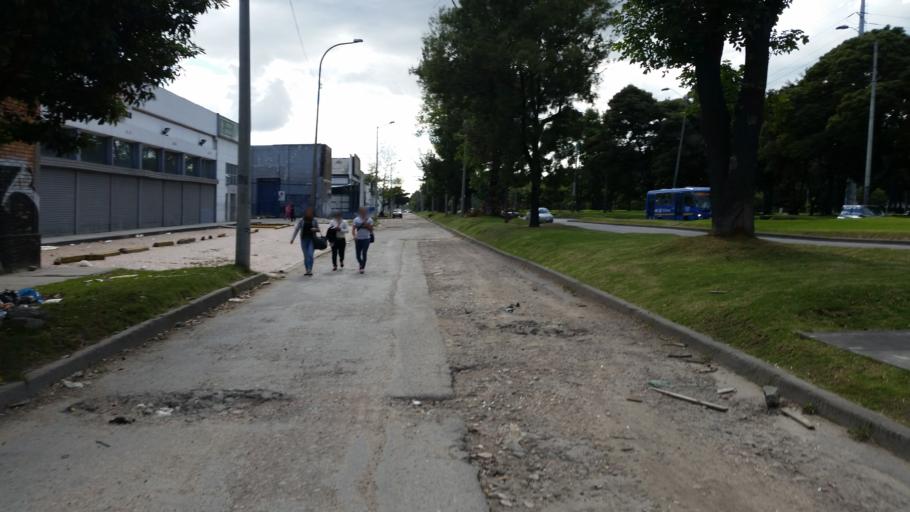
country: CO
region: Bogota D.C.
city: Bogota
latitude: 4.6247
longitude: -74.0861
